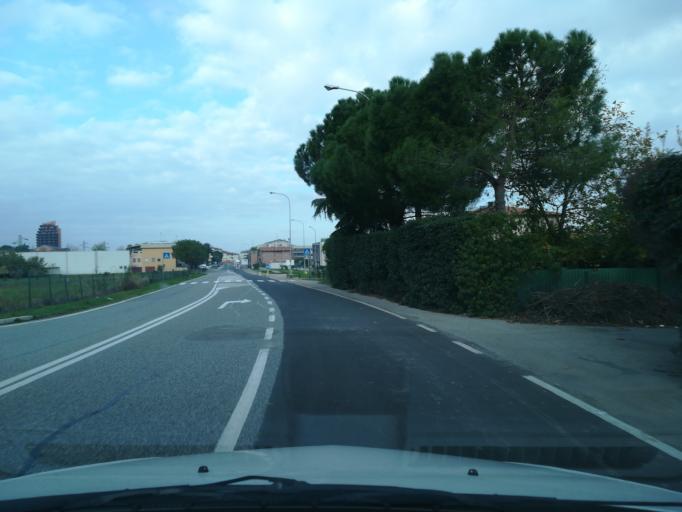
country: IT
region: Emilia-Romagna
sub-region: Provincia di Bologna
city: Imola
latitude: 44.3597
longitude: 11.7300
